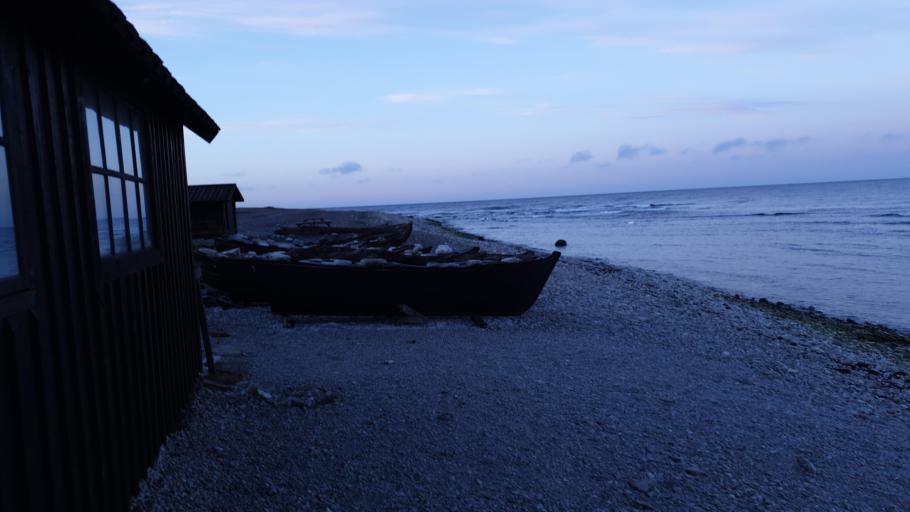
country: SE
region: Gotland
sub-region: Gotland
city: Slite
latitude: 57.9805
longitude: 19.1328
